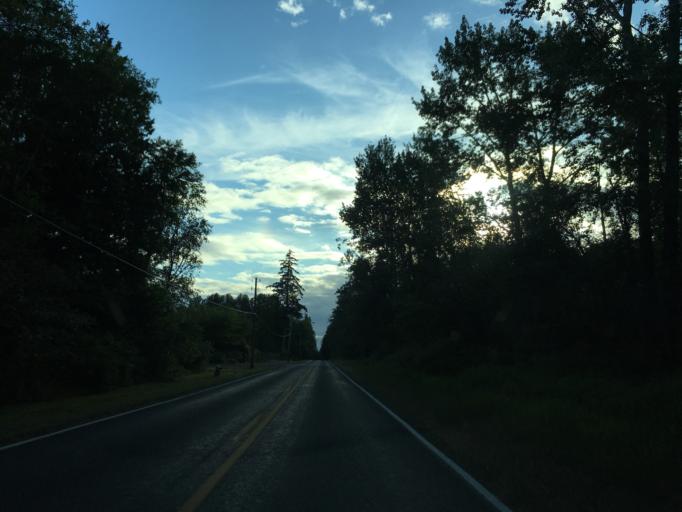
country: US
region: Washington
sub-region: Whatcom County
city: Birch Bay
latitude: 48.9405
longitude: -122.8080
